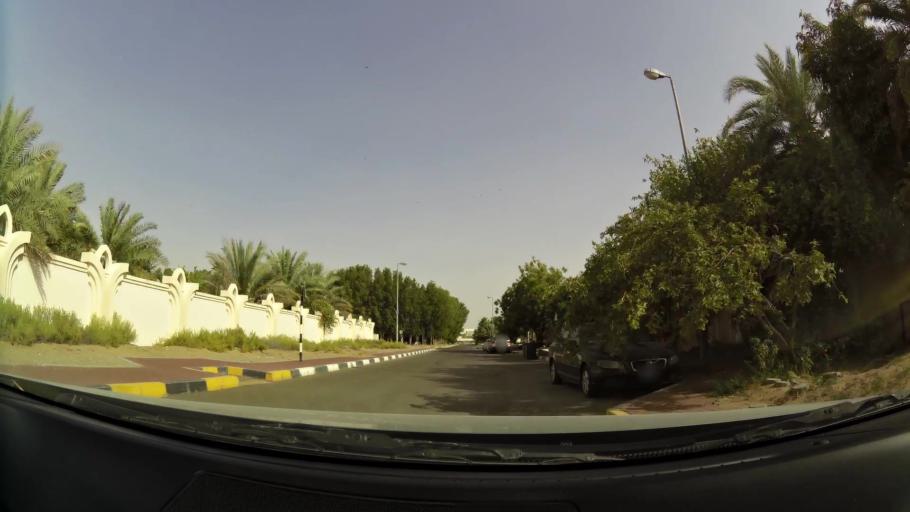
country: AE
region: Abu Dhabi
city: Al Ain
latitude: 24.2278
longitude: 55.6576
